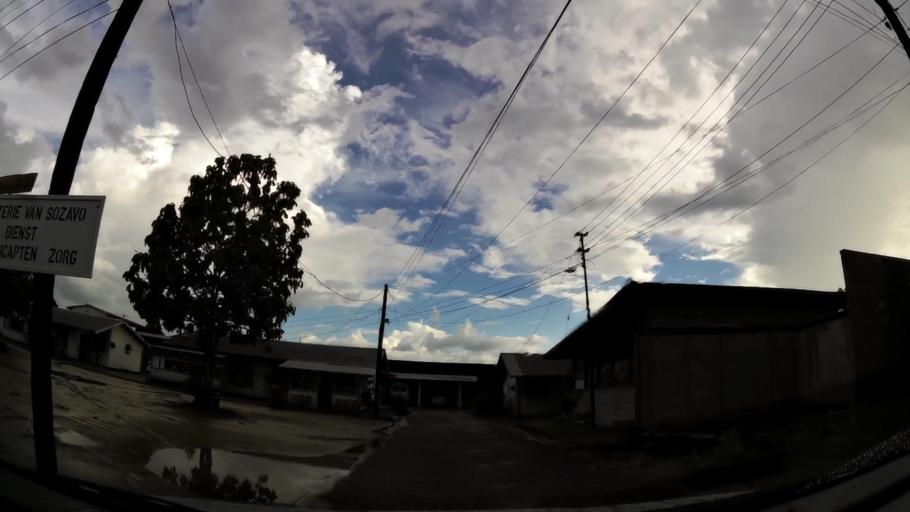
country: SR
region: Paramaribo
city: Paramaribo
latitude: 5.8245
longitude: -55.1830
